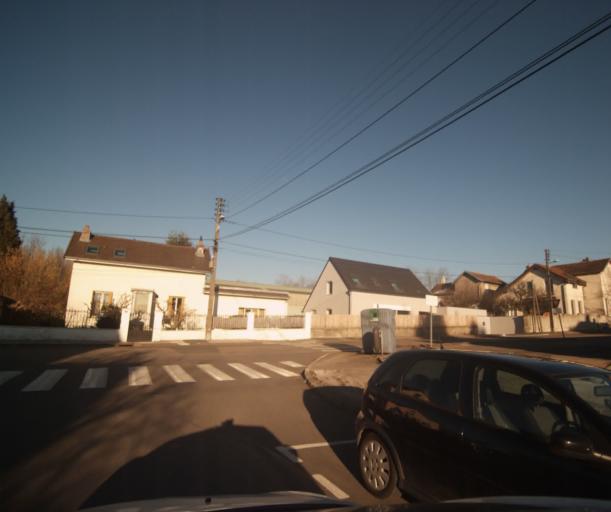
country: FR
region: Franche-Comte
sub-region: Departement du Doubs
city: Besancon
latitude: 47.2582
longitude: 6.0136
